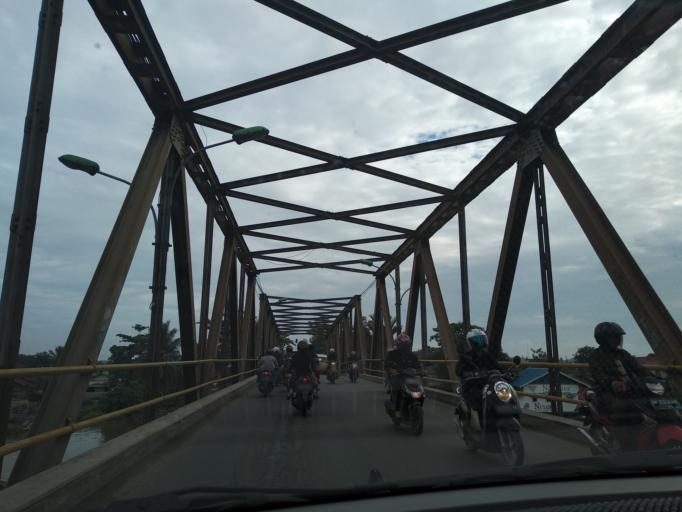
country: ID
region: South Kalimantan
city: Banjarmasin
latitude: -3.2774
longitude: 114.5899
